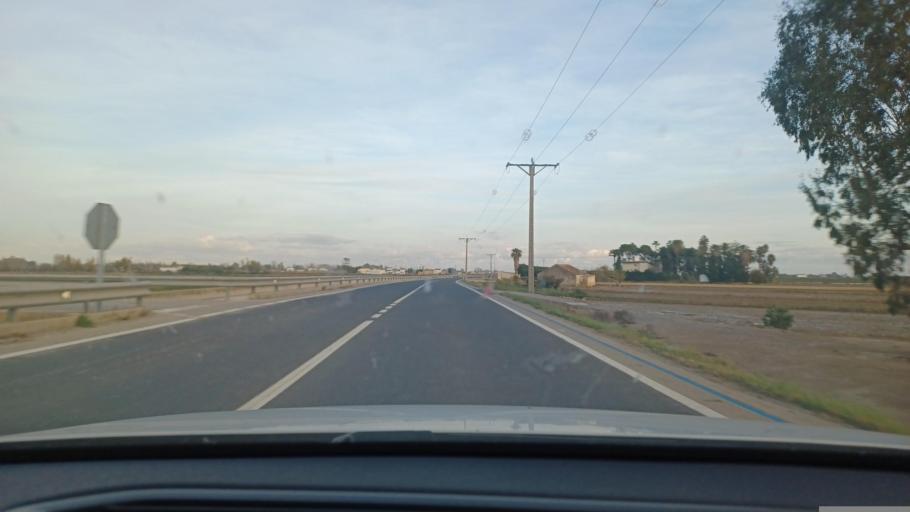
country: ES
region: Catalonia
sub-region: Provincia de Tarragona
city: Deltebre
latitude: 40.7110
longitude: 0.6734
